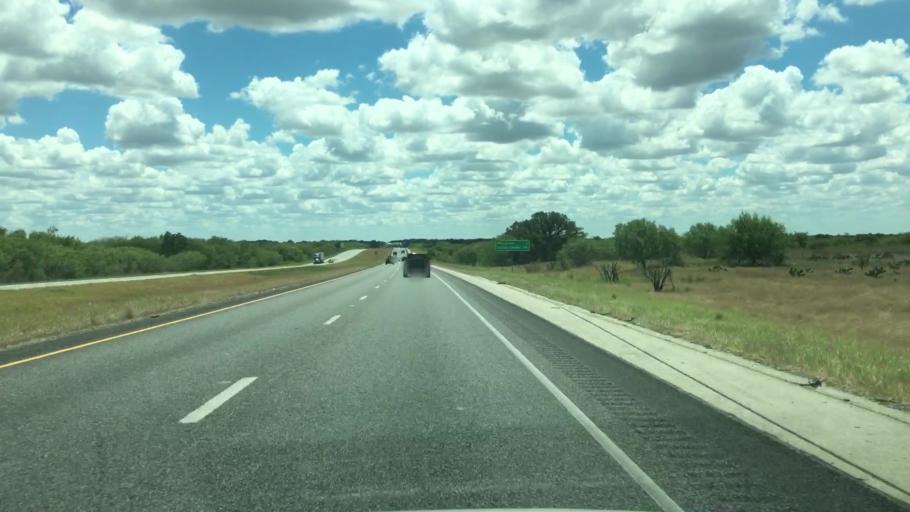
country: US
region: Texas
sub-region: Atascosa County
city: Pleasanton
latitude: 29.0934
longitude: -98.4331
